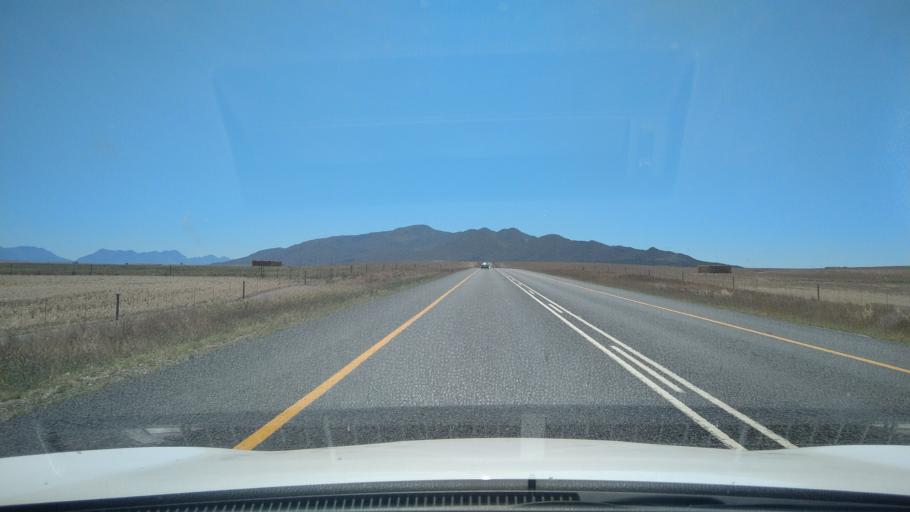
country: ZA
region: Western Cape
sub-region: Overberg District Municipality
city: Caledon
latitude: -34.2117
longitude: 19.3628
